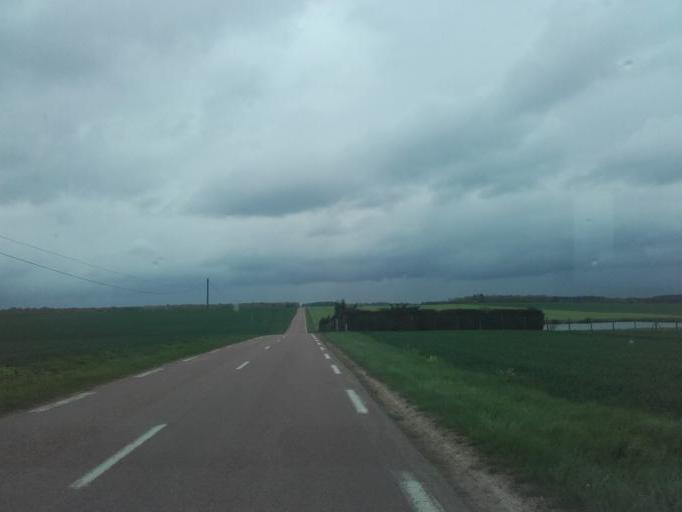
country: FR
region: Bourgogne
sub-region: Departement de l'Yonne
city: Joux-la-Ville
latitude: 47.6793
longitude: 3.8725
